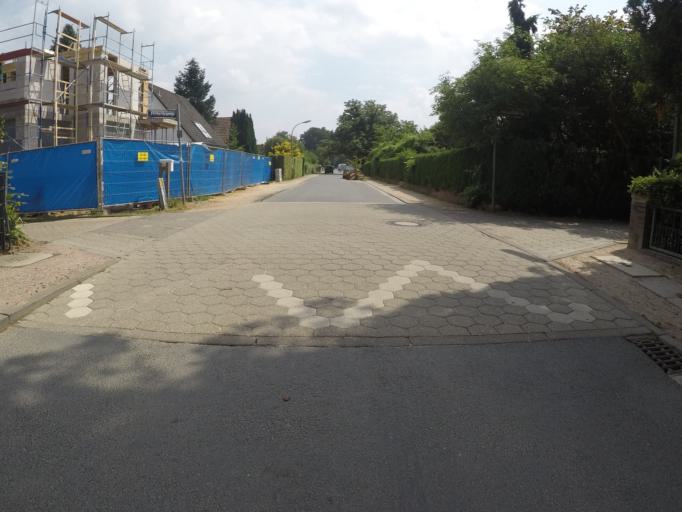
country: DE
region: Hamburg
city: Sasel
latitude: 53.6471
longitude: 10.1158
